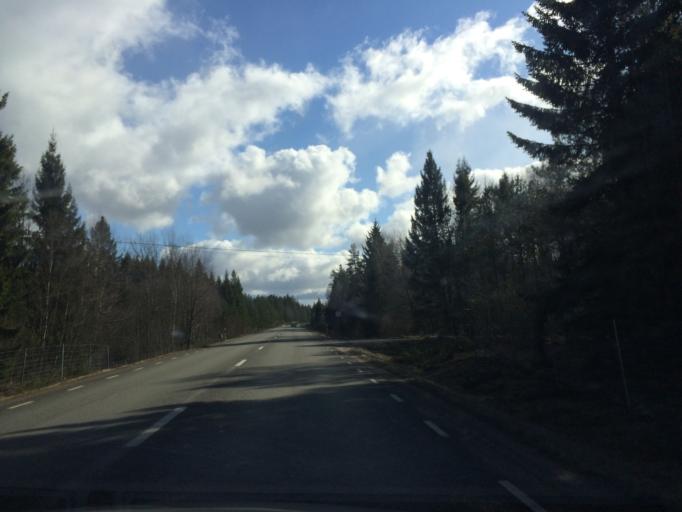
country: SE
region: Vaestra Goetaland
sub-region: Skara Kommun
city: Skara
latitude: 58.3598
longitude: 13.4242
